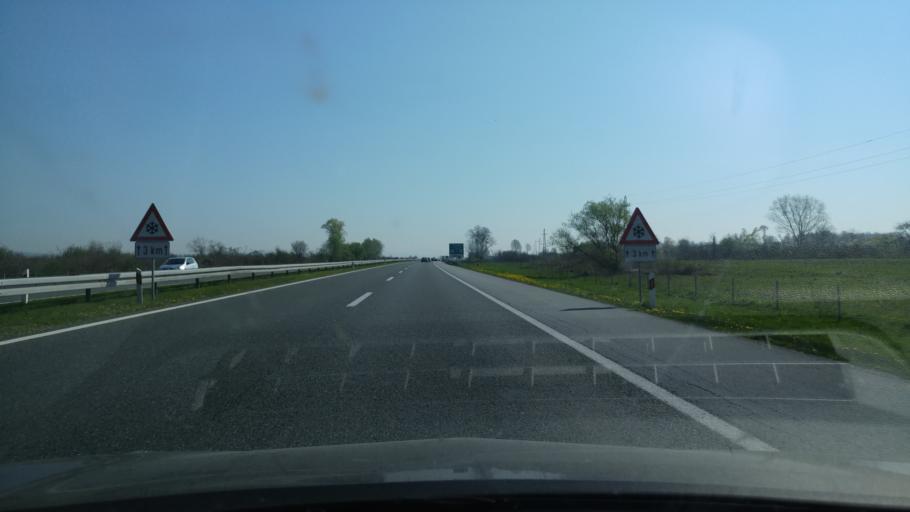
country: HR
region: Brodsko-Posavska
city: Okucani
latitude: 45.2321
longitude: 17.2554
